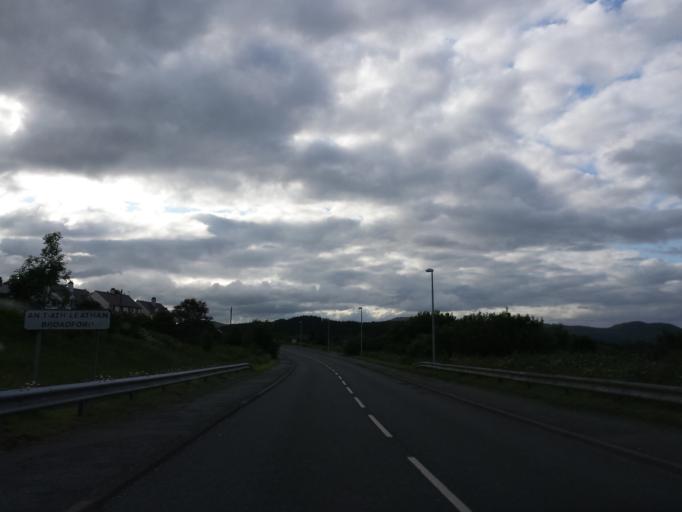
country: GB
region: Scotland
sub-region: Highland
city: Portree
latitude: 57.2392
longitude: -5.8986
